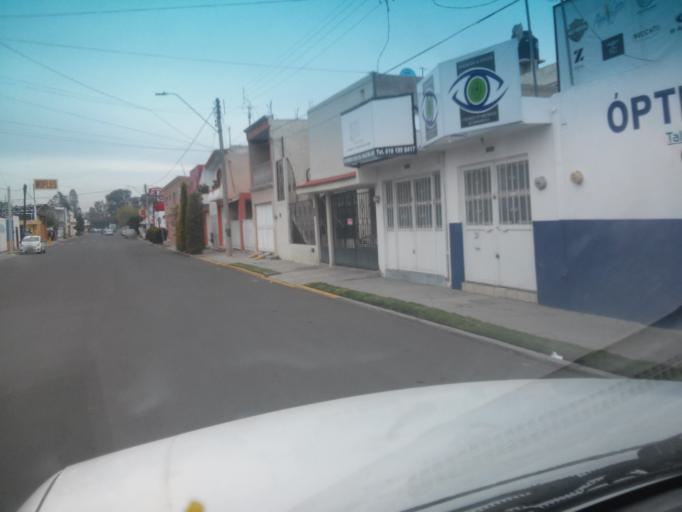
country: MX
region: Durango
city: Victoria de Durango
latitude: 24.0125
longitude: -104.6795
